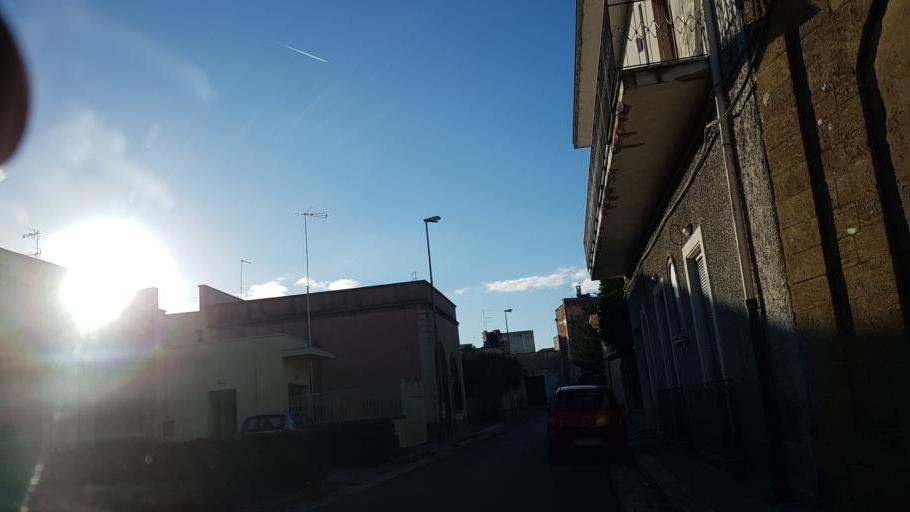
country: IT
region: Apulia
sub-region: Provincia di Lecce
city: Squinzano
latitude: 40.4356
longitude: 18.0476
